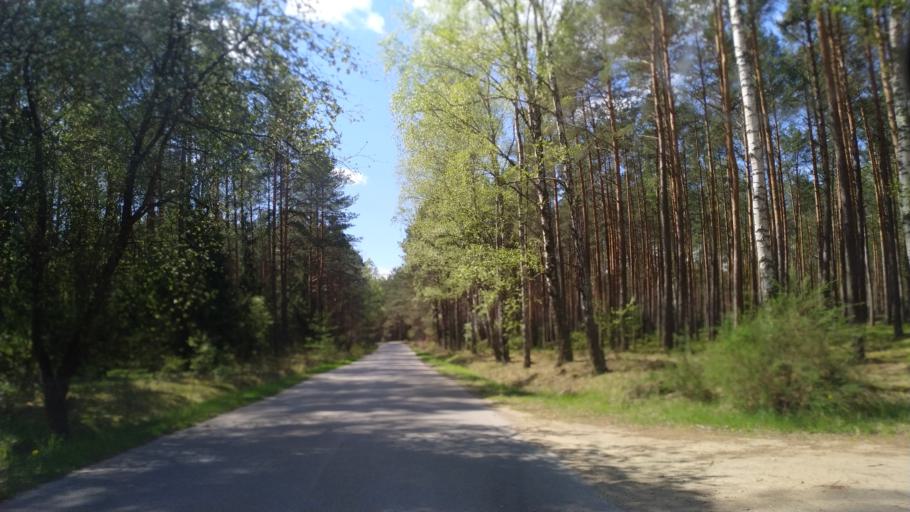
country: PL
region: Greater Poland Voivodeship
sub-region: Powiat pilski
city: Pila
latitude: 53.2484
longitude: 16.7152
